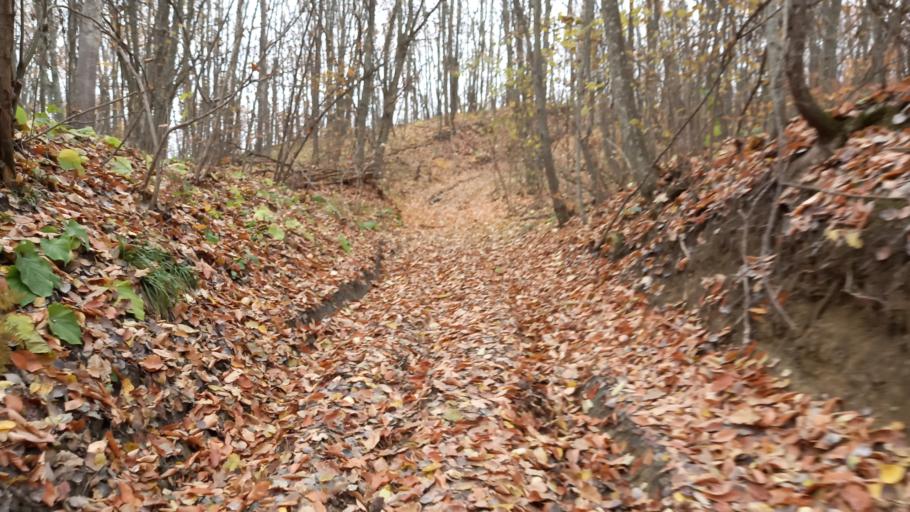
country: RU
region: Krasnodarskiy
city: Goryachiy Klyuch
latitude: 44.4945
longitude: 39.2751
